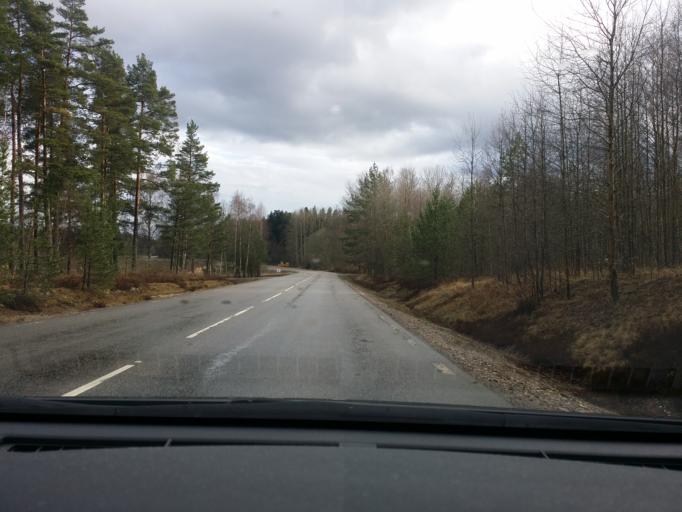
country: SE
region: Soedermanland
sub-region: Eskilstuna Kommun
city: Arla
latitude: 59.3209
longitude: 16.6796
